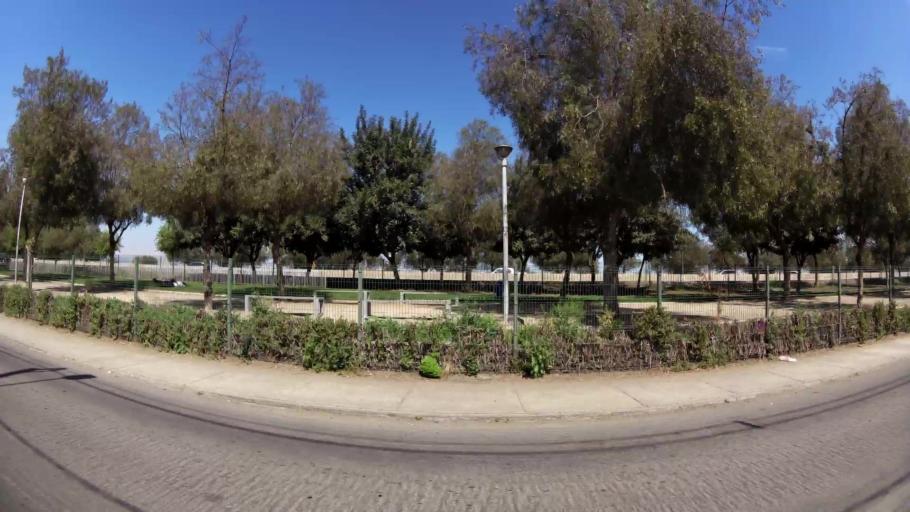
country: CL
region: Santiago Metropolitan
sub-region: Provincia de Santiago
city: Lo Prado
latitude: -33.4114
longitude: -70.7420
